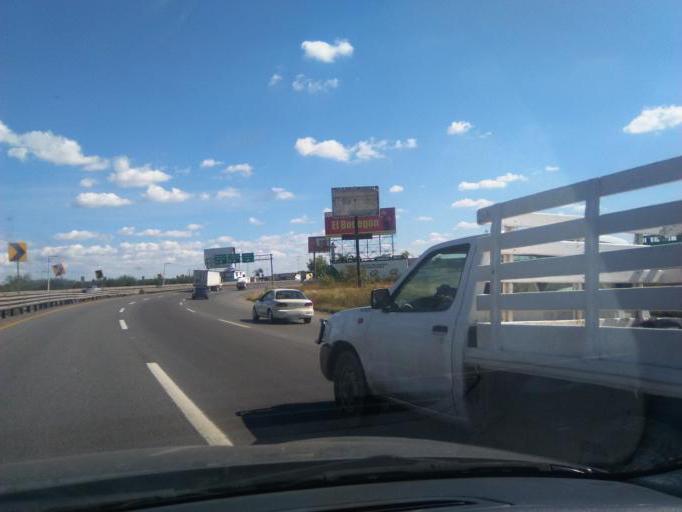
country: MX
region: Guanajuato
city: Silao
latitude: 20.9545
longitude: -101.4164
